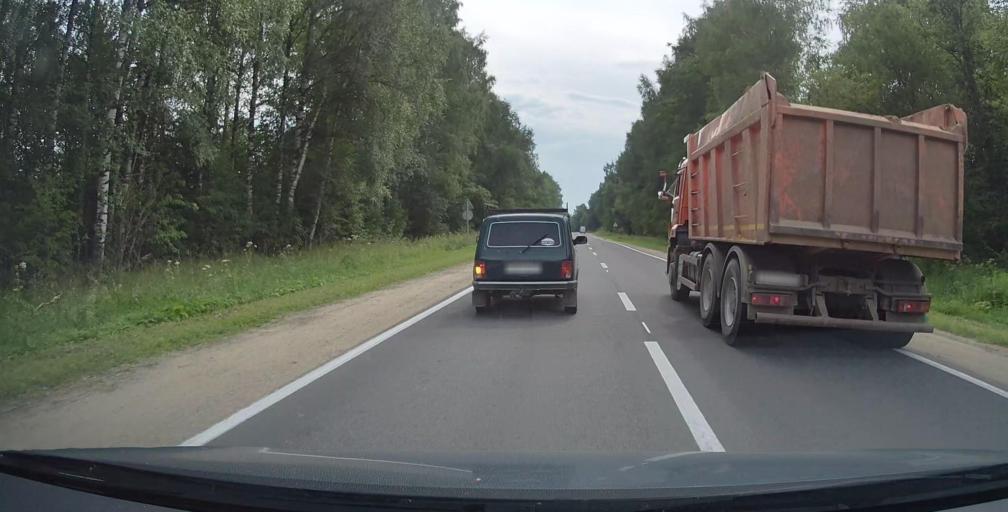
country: RU
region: Jaroslavl
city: Rybinsk
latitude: 57.9912
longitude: 38.7538
